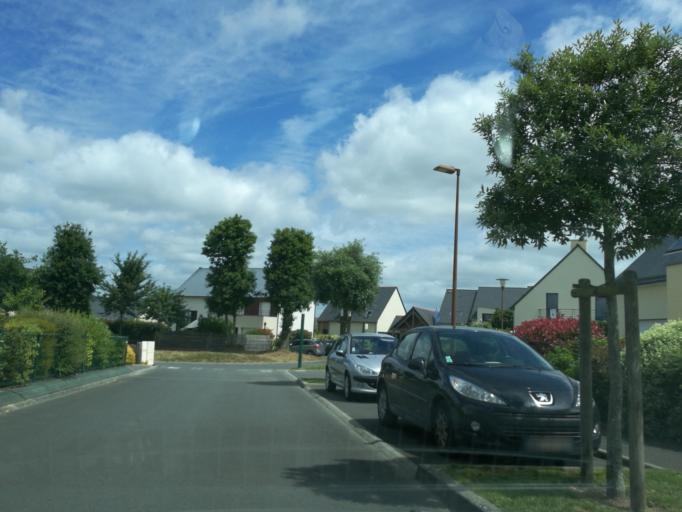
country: FR
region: Brittany
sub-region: Departement d'Ille-et-Vilaine
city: Bedee
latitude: 48.1745
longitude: -1.9419
